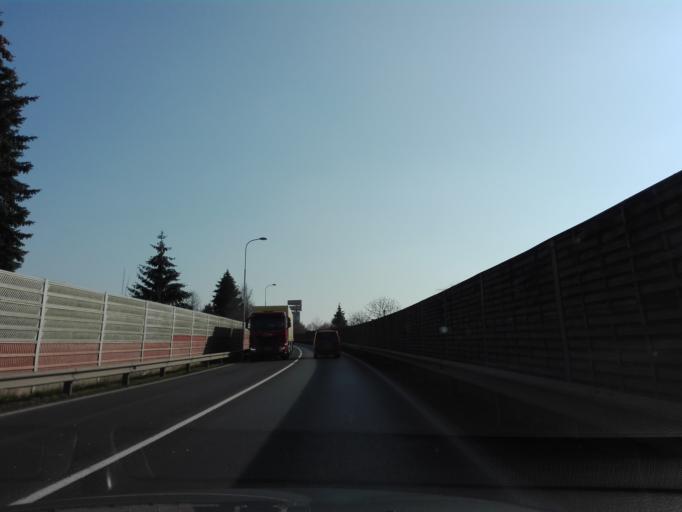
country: AT
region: Upper Austria
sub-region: Politischer Bezirk Linz-Land
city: Traun
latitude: 48.2016
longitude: 14.2470
